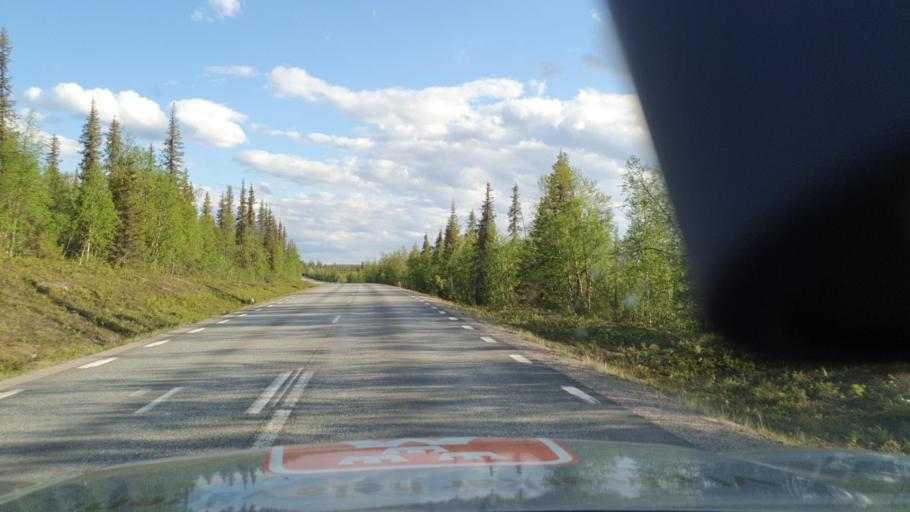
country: SE
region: Norrbotten
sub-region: Gallivare Kommun
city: Malmberget
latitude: 67.3173
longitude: 21.0815
